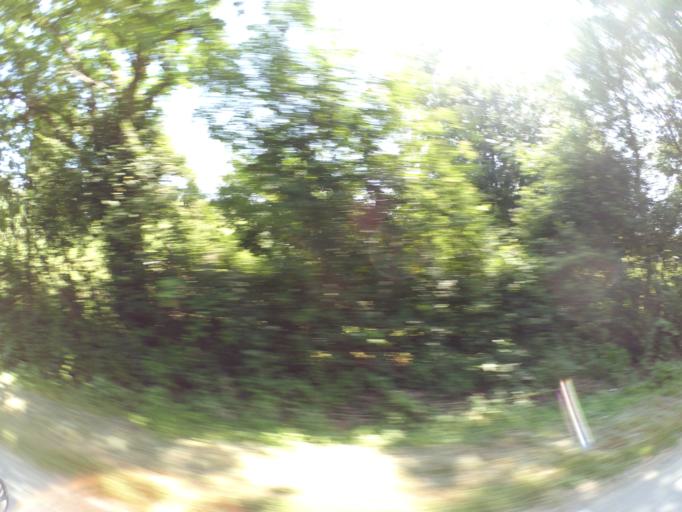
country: FR
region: Pays de la Loire
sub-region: Departement de la Vendee
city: Saint-Michel-Mont-Mercure
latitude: 46.8233
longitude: -0.8772
